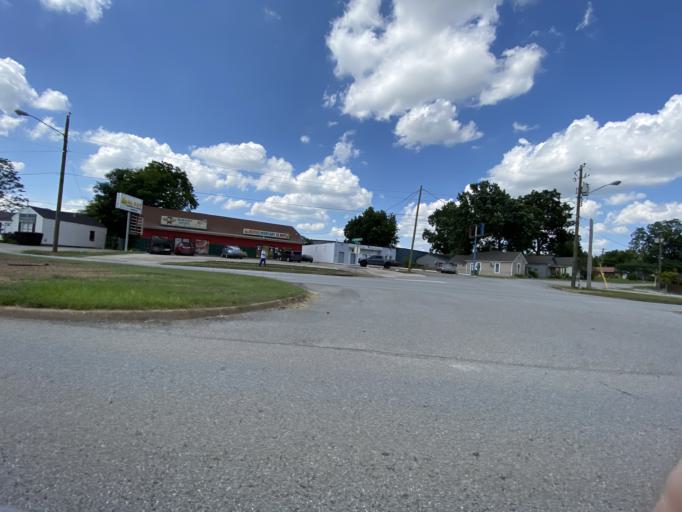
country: US
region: Alabama
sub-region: Madison County
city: Huntsville
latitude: 34.7200
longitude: -86.6056
